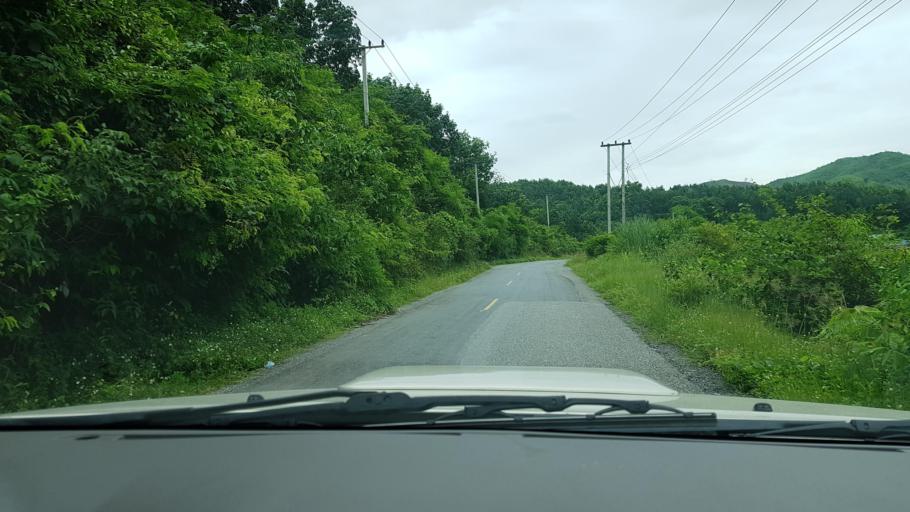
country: LA
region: Loungnamtha
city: Muang Nale
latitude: 20.1961
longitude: 101.5270
